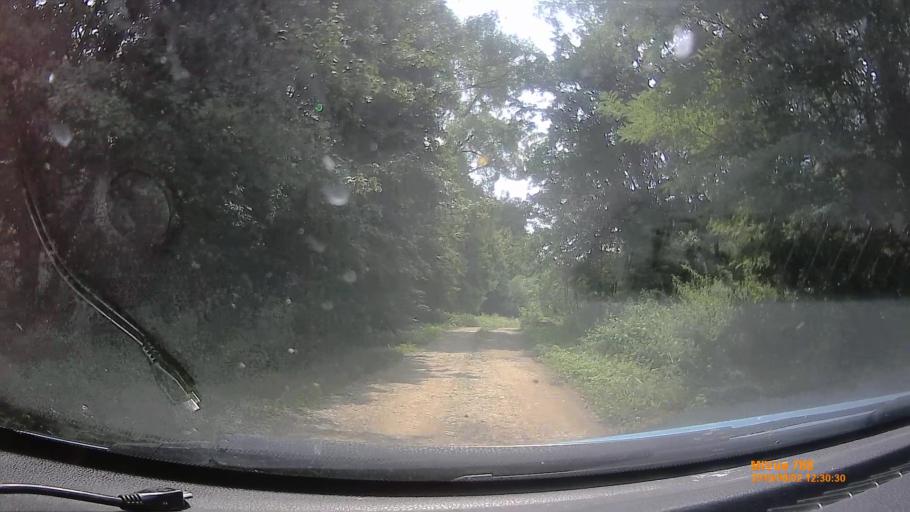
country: HU
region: Baranya
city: Buekkoesd
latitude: 46.1088
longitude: 17.9352
